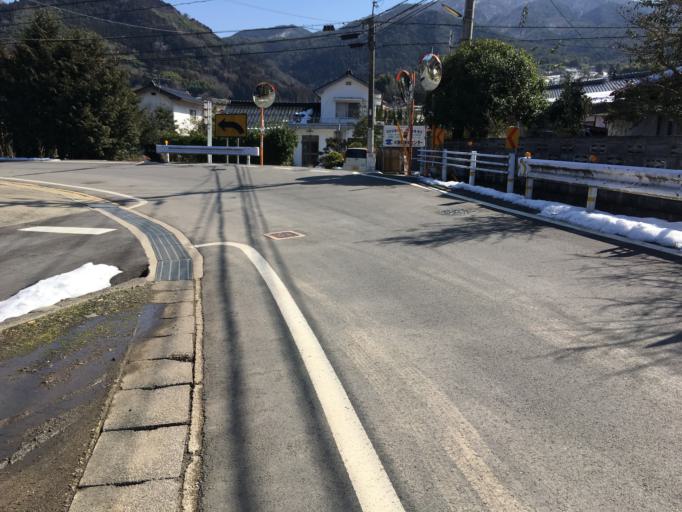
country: JP
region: Shimane
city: Masuda
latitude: 34.4518
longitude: 131.7630
